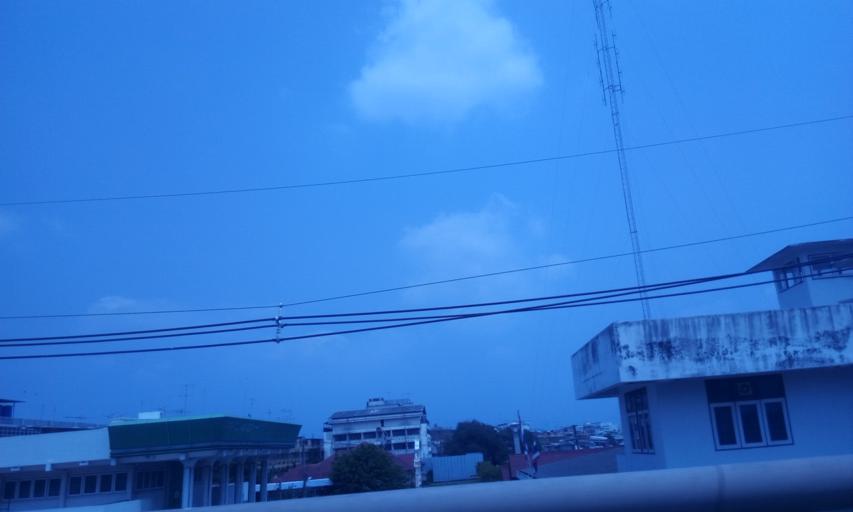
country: TH
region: Chachoengsao
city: Chachoengsao
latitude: 13.6891
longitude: 101.0765
